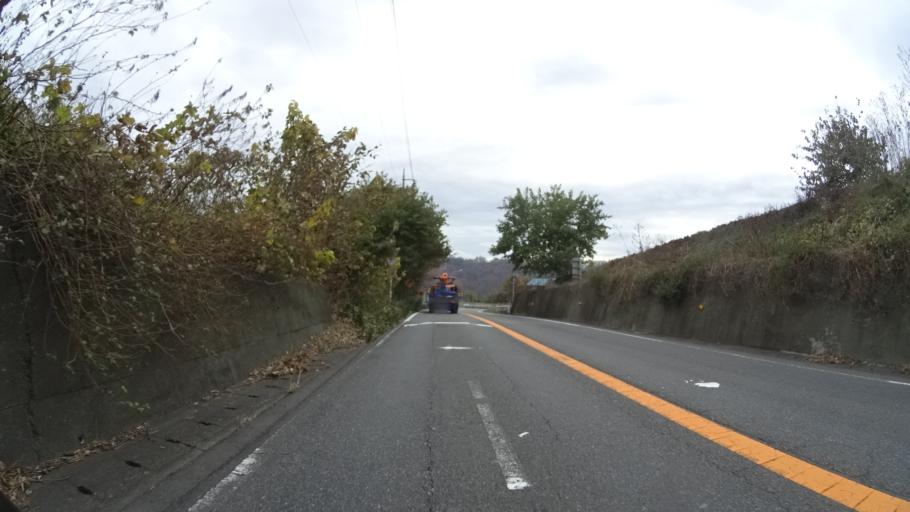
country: JP
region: Gunma
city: Numata
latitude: 36.5746
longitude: 139.0498
